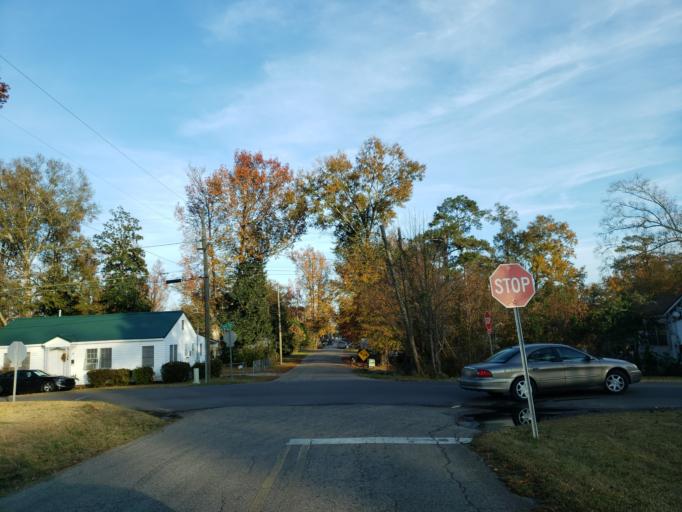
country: US
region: Mississippi
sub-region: Forrest County
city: Hattiesburg
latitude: 31.3284
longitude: -89.3178
